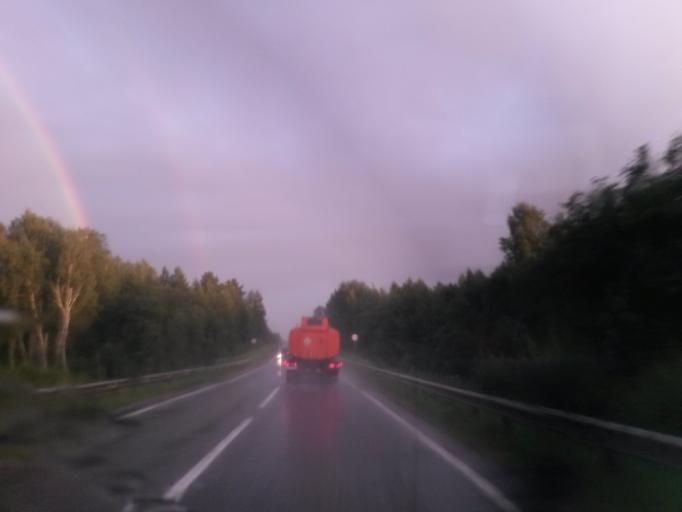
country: RU
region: Jaroslavl
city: Gavrilov-Yam
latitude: 57.3722
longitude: 39.9073
